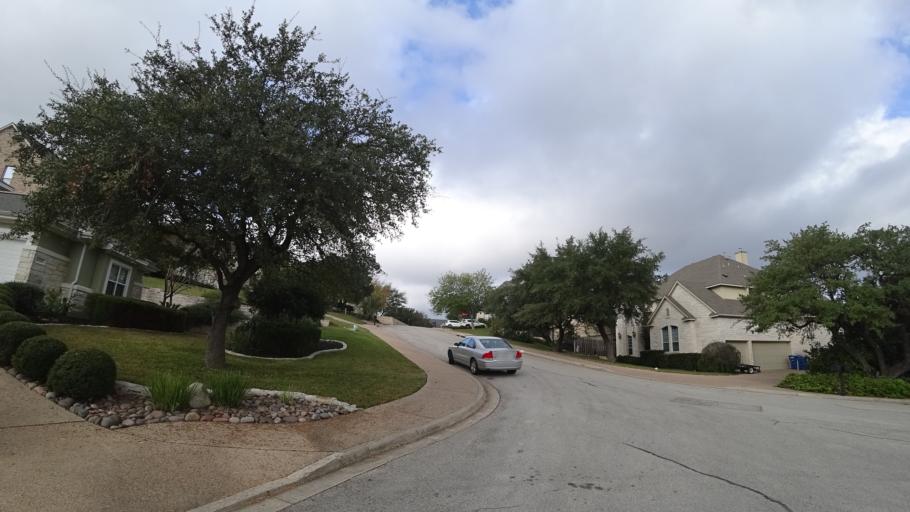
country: US
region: Texas
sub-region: Travis County
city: Barton Creek
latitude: 30.3138
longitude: -97.8955
